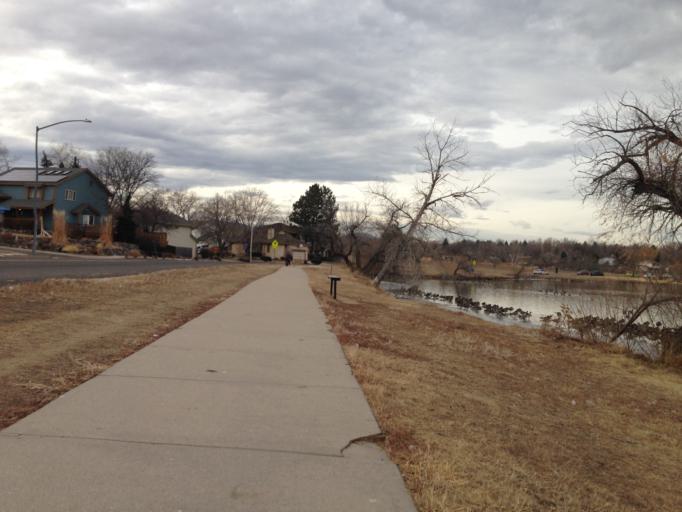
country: US
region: Colorado
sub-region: Adams County
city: Westminster
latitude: 39.8428
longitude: -105.0695
